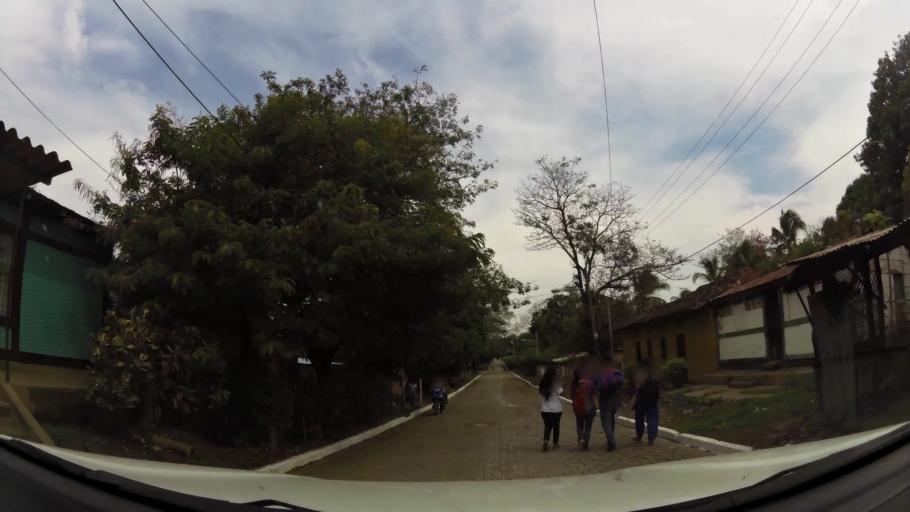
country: NI
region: Rivas
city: Rivas
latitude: 11.4351
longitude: -85.8326
